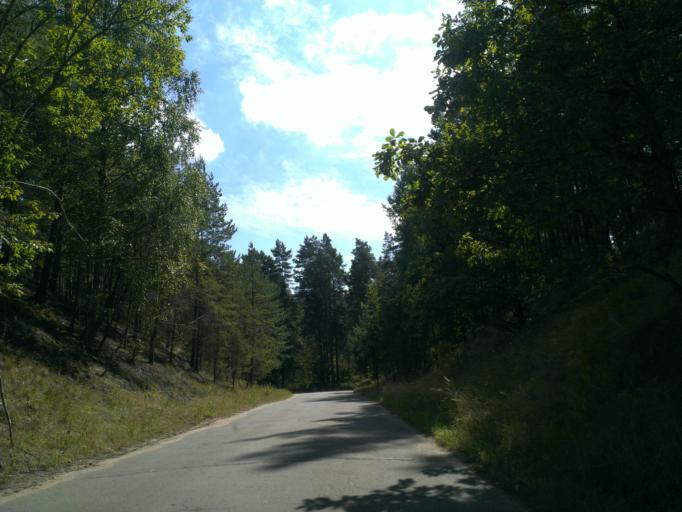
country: LV
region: Adazi
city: Adazi
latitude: 57.0874
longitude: 24.3440
